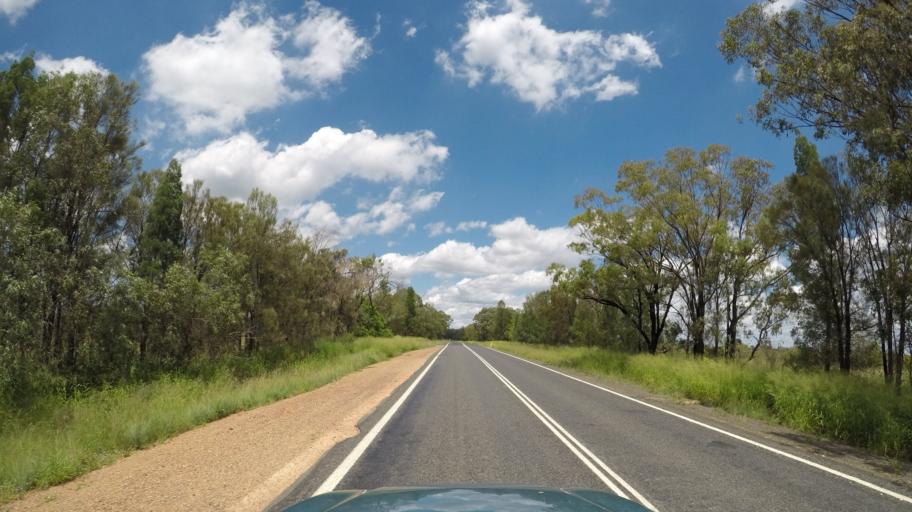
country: AU
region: Queensland
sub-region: Western Downs
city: Dalby
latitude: -27.9633
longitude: 151.1191
